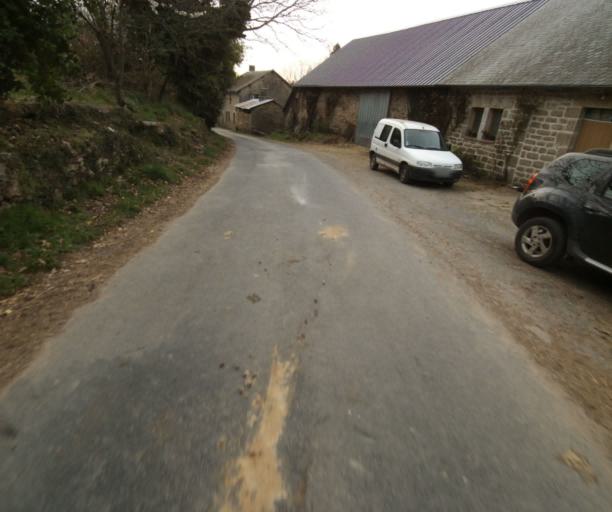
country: FR
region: Limousin
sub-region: Departement de la Correze
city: Correze
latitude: 45.4382
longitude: 1.8235
